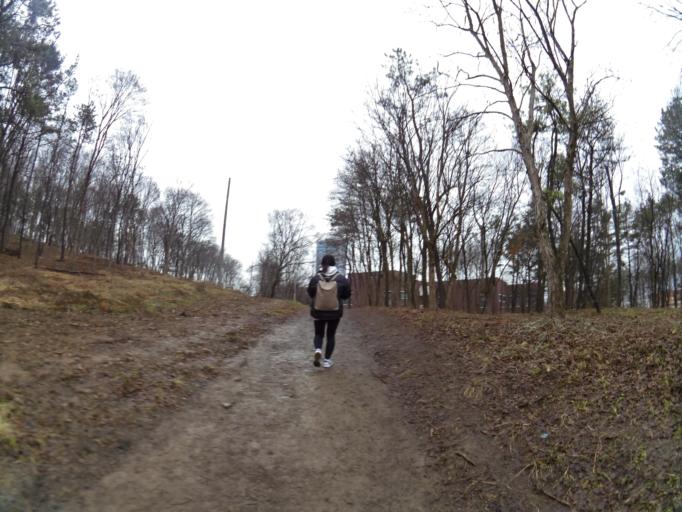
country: KR
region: Gyeongsangbuk-do
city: Gyeongsan-si
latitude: 35.8360
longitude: 128.7574
